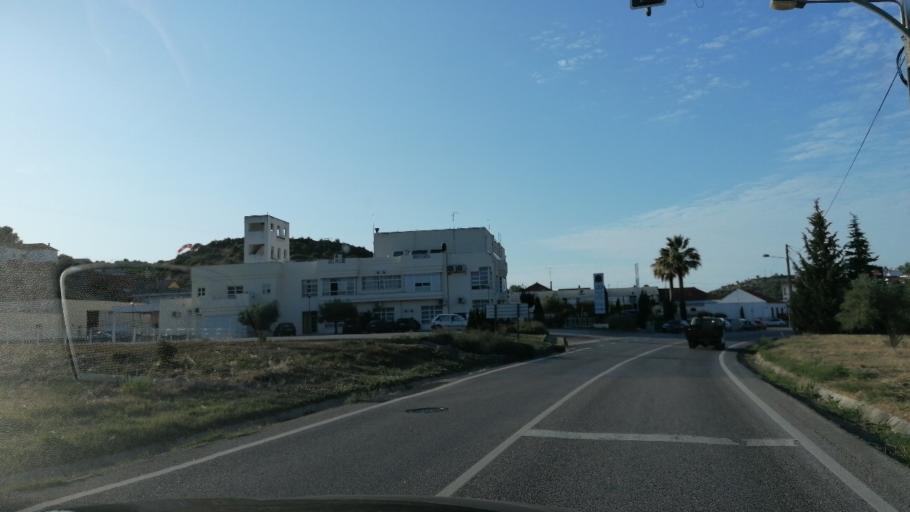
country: PT
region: Santarem
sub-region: Alcanena
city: Alcanena
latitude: 39.3760
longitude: -8.6608
